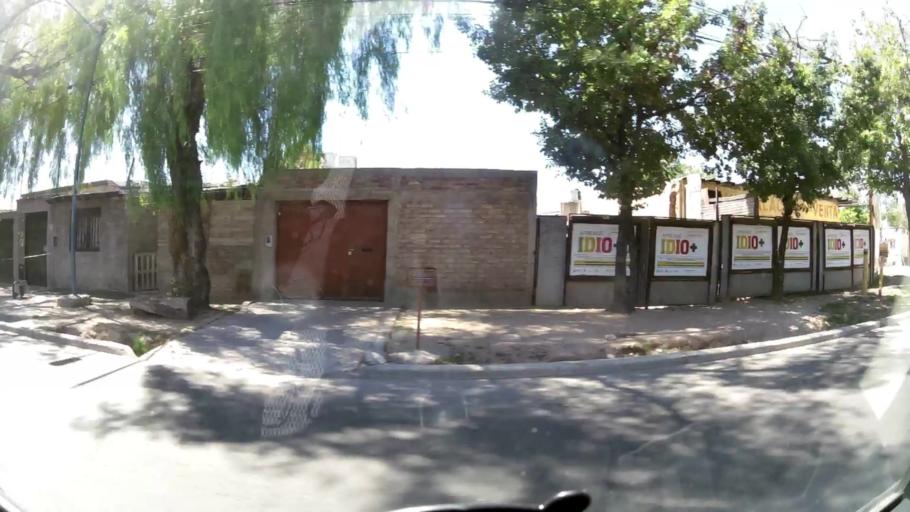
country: AR
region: Mendoza
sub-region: Departamento de Godoy Cruz
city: Godoy Cruz
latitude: -32.9128
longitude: -68.8640
